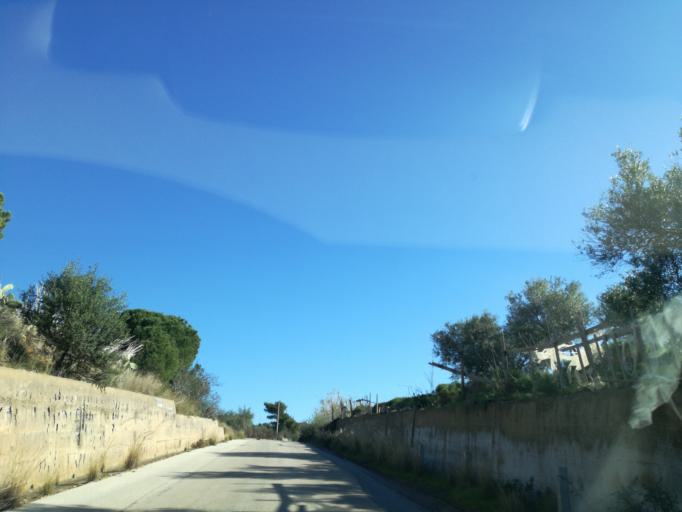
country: IT
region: Sicily
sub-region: Provincia di Caltanissetta
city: Niscemi
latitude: 37.0607
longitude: 14.3485
